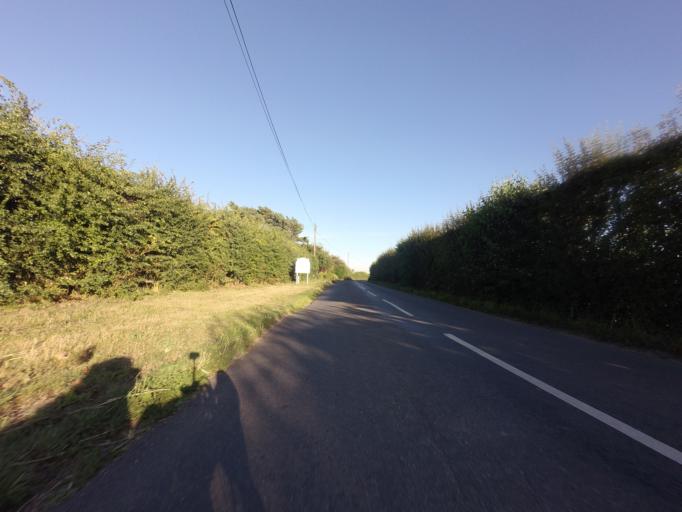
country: GB
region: England
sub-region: Kent
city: Herne Bay
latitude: 51.3489
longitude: 1.1844
